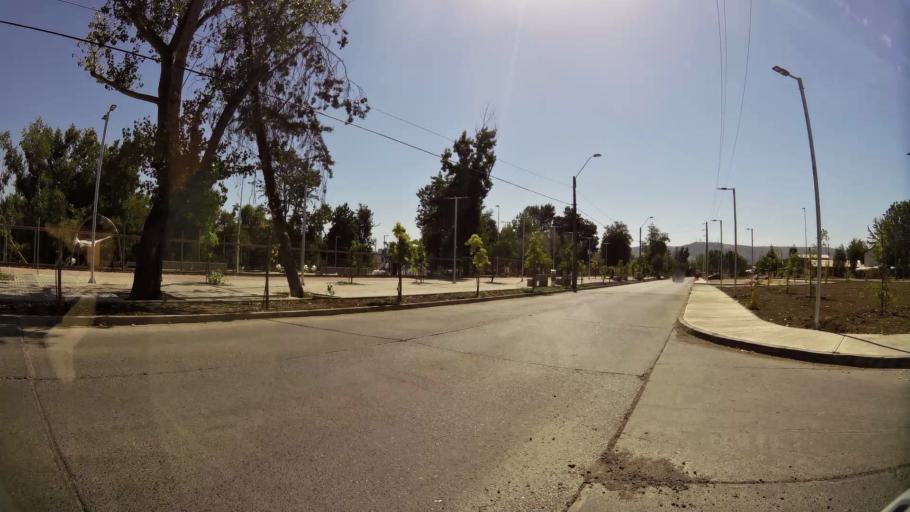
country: CL
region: Maule
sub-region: Provincia de Talca
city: Talca
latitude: -35.4365
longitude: -71.6611
